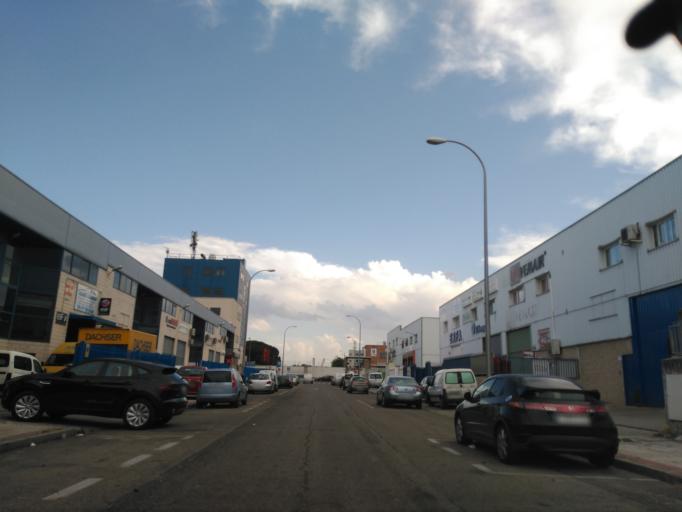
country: ES
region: Madrid
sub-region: Provincia de Madrid
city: Villaverde
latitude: 40.3347
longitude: -3.7140
